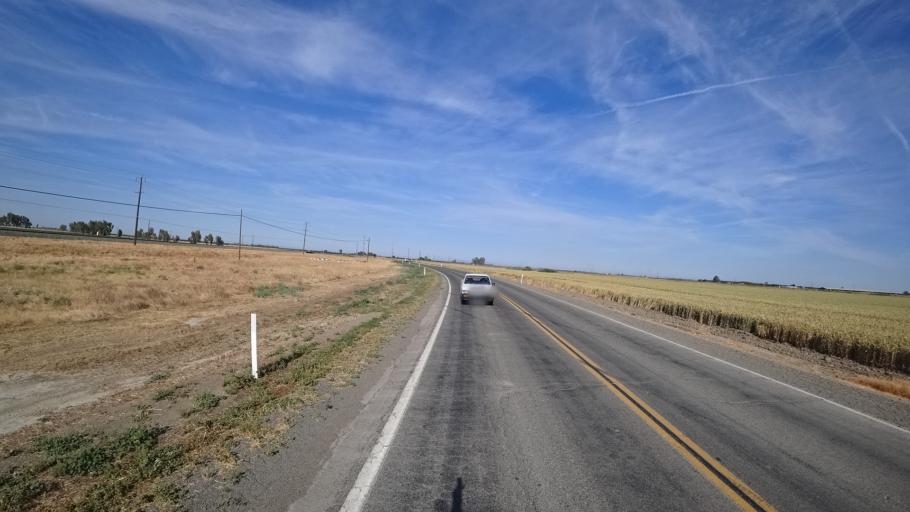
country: US
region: California
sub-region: Kings County
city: Home Garden
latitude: 36.3432
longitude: -119.5324
